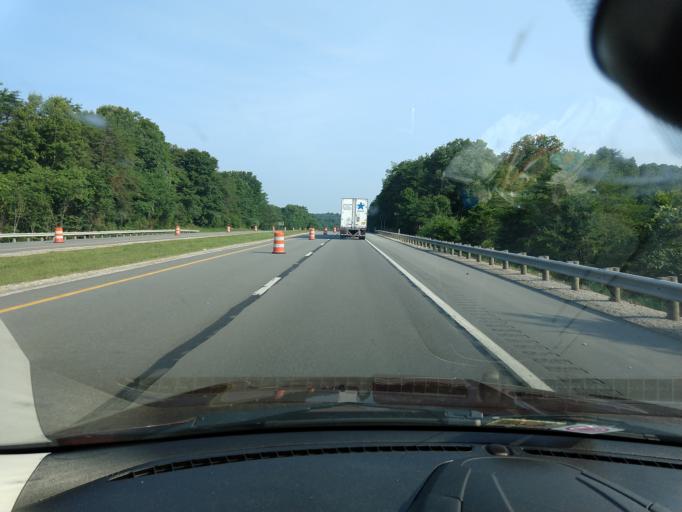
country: US
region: West Virginia
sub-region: Jackson County
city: Ripley
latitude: 38.7864
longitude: -81.7258
